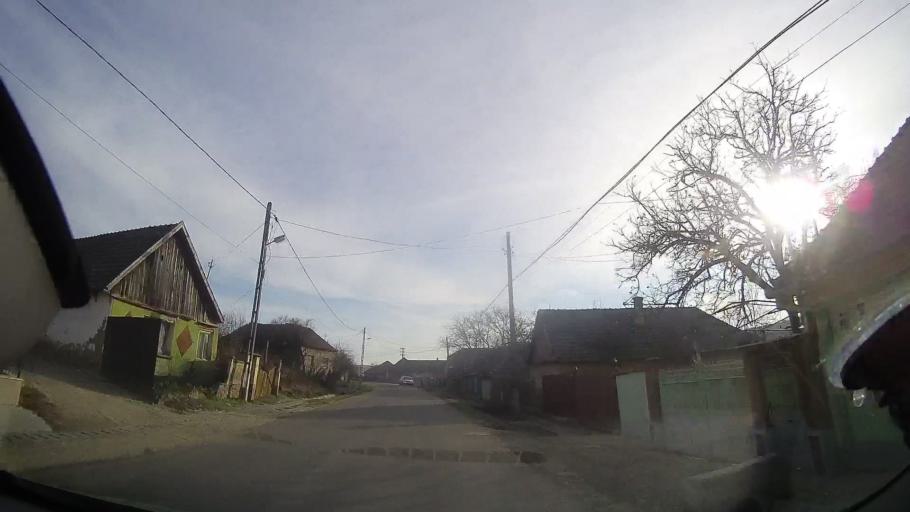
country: RO
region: Bihor
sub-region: Comuna Sarbi
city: Sarbi
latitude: 47.1899
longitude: 22.1248
